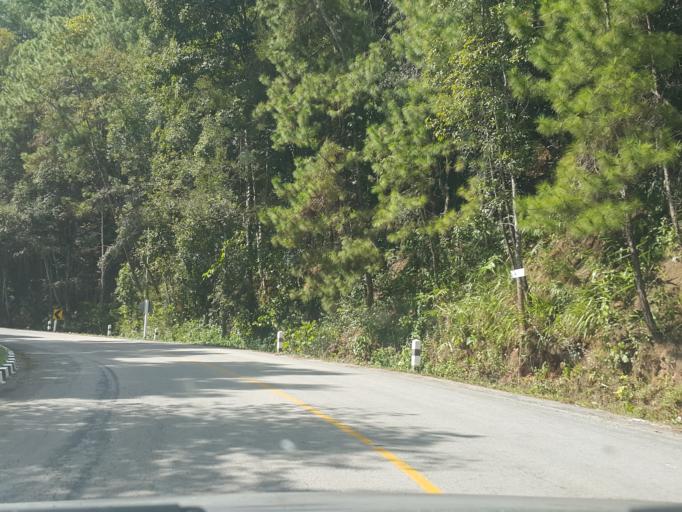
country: TH
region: Mae Hong Son
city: Mae Hi
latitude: 19.2623
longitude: 98.6360
